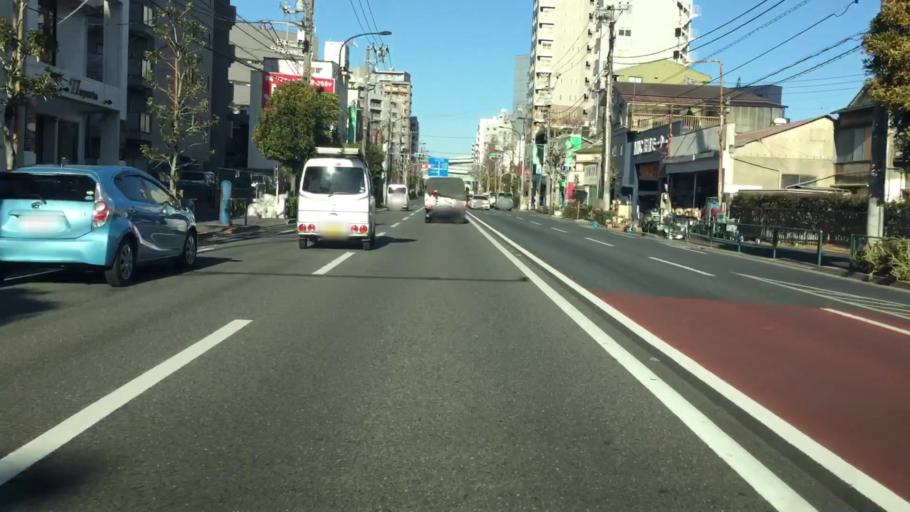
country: JP
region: Saitama
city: Kawaguchi
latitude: 35.7515
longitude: 139.7473
